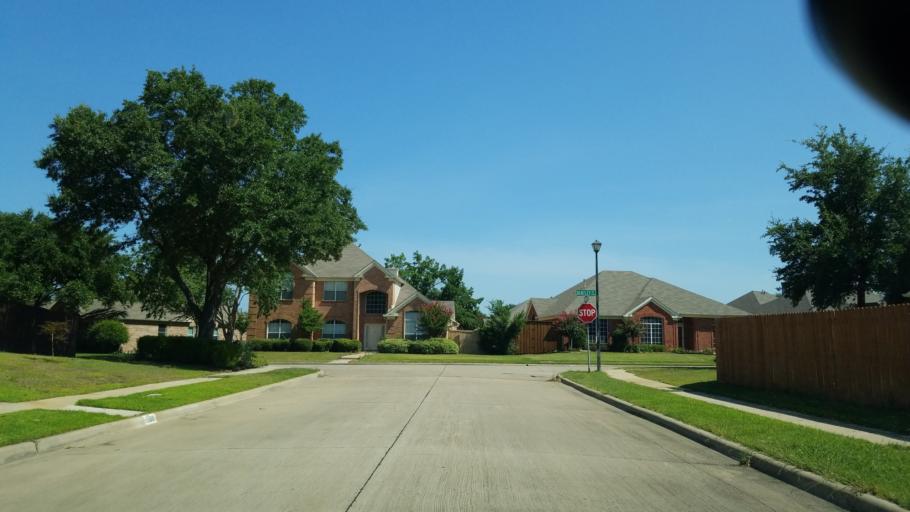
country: US
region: Texas
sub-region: Dallas County
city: Carrollton
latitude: 32.9691
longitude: -96.8977
